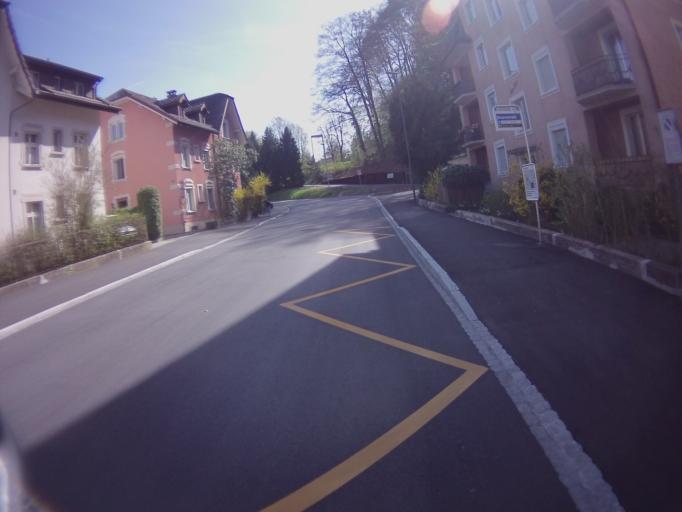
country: CH
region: Aargau
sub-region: Bezirk Baden
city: Baden
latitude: 47.4638
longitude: 8.3062
